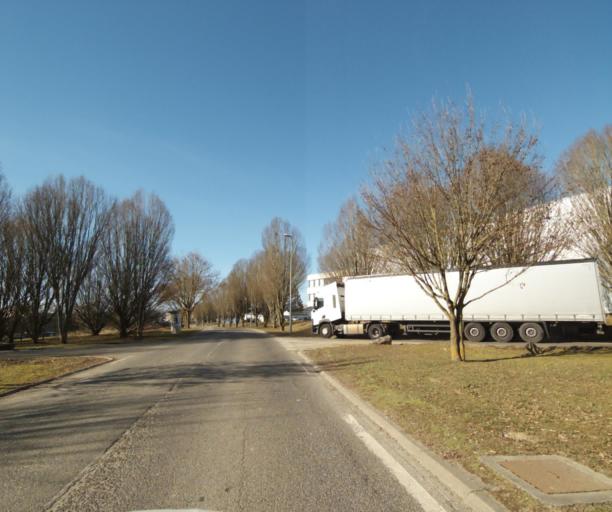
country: FR
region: Lorraine
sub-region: Departement de Meurthe-et-Moselle
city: Fleville-devant-Nancy
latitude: 48.6189
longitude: 6.1923
